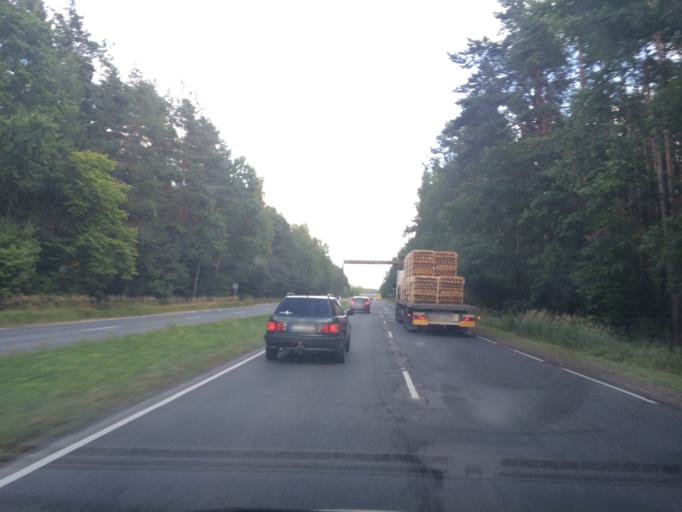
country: LV
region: Salaspils
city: Salaspils
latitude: 56.8619
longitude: 24.2990
